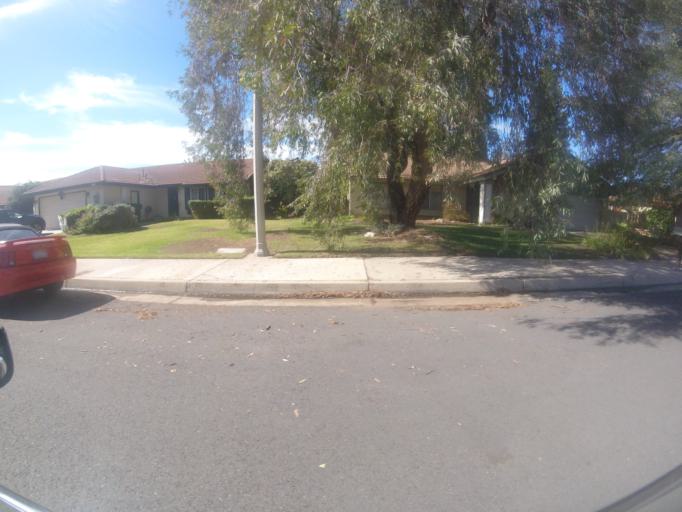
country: US
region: California
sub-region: San Bernardino County
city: Mentone
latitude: 34.0621
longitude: -117.1485
